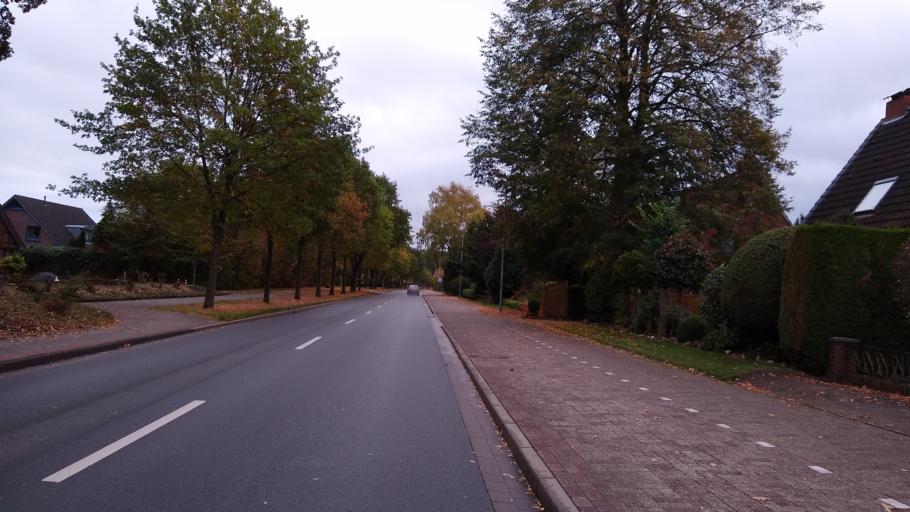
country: DE
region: Lower Saxony
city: Rastede
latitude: 53.2078
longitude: 8.2342
